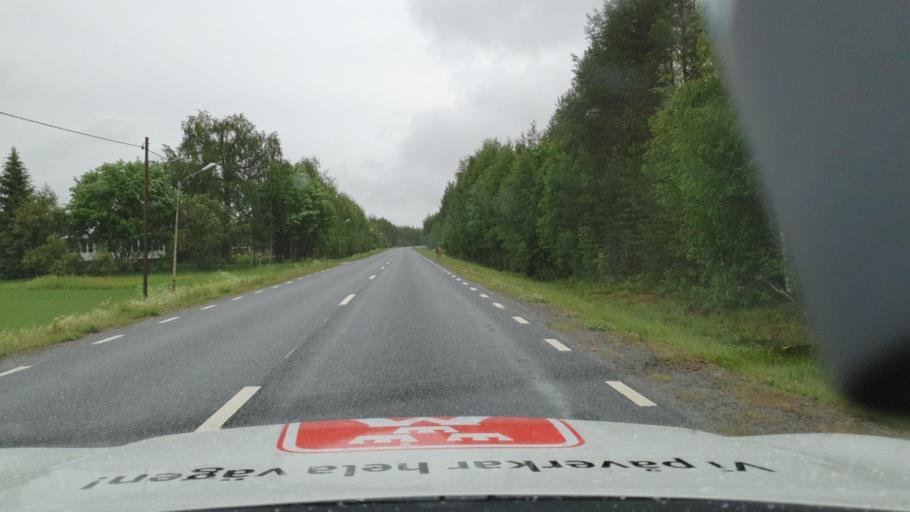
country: SE
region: Vaesterbotten
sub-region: Asele Kommun
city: Asele
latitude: 64.0325
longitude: 17.2961
